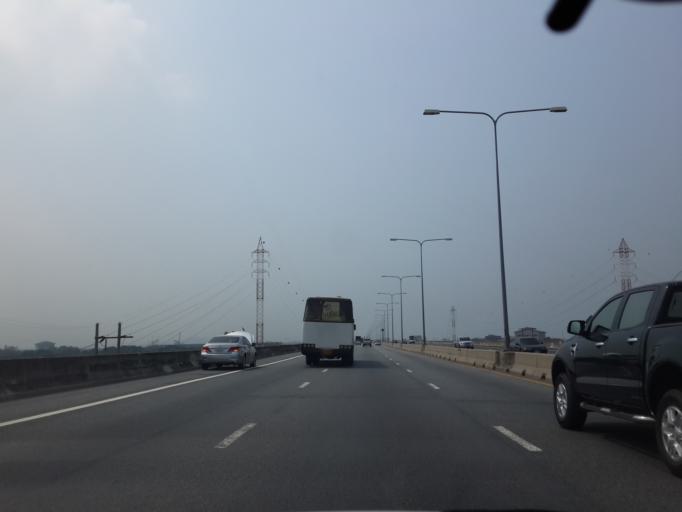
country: TH
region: Chachoengsao
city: Bang Pakong
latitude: 13.4895
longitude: 101.0052
